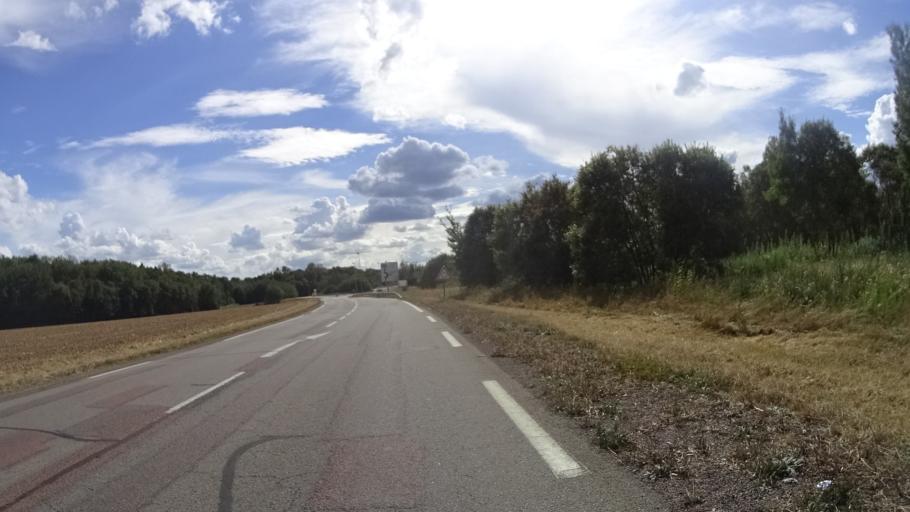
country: FR
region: Bourgogne
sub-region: Departement de la Cote-d'Or
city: Seurre
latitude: 47.0373
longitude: 5.1819
